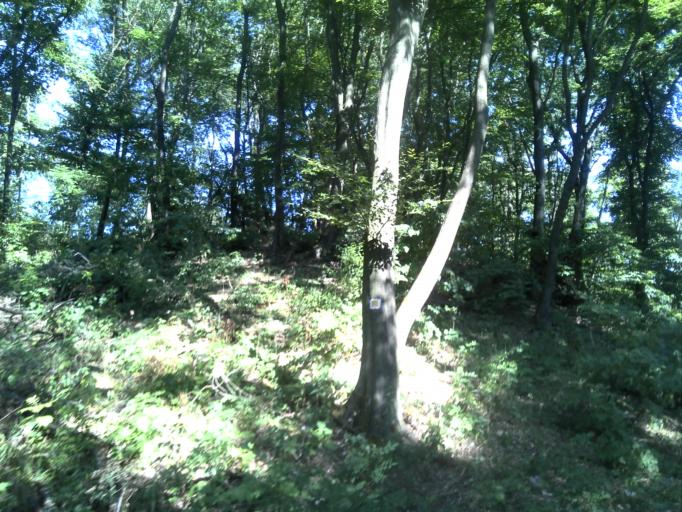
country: HU
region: Pest
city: Piliscsaba
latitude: 47.6324
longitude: 18.8620
